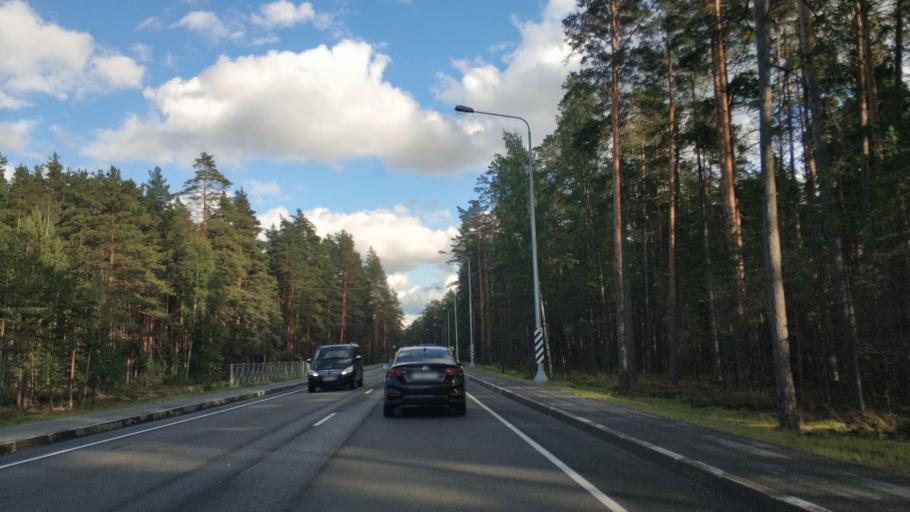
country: RU
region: Leningrad
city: Priozersk
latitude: 61.0126
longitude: 30.1549
